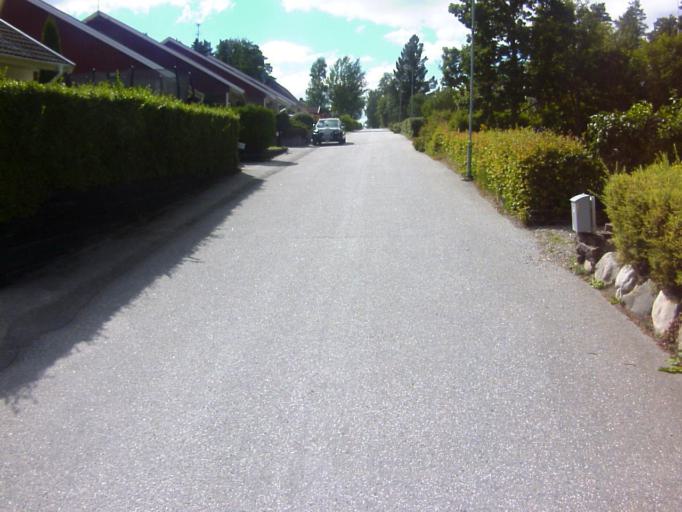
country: SE
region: Soedermanland
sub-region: Eskilstuna Kommun
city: Hallbybrunn
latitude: 59.3446
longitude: 16.4348
